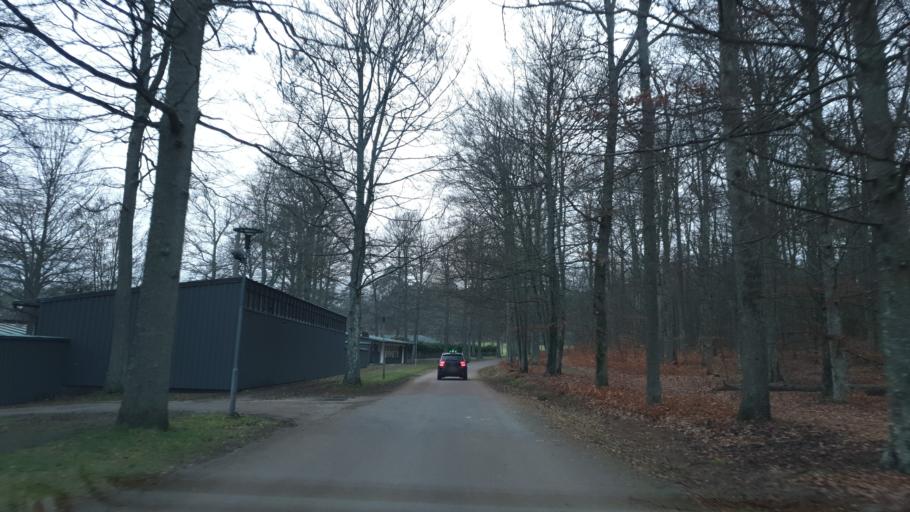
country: SE
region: Blekinge
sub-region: Karlskrona Kommun
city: Rodeby
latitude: 56.2148
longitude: 15.6837
